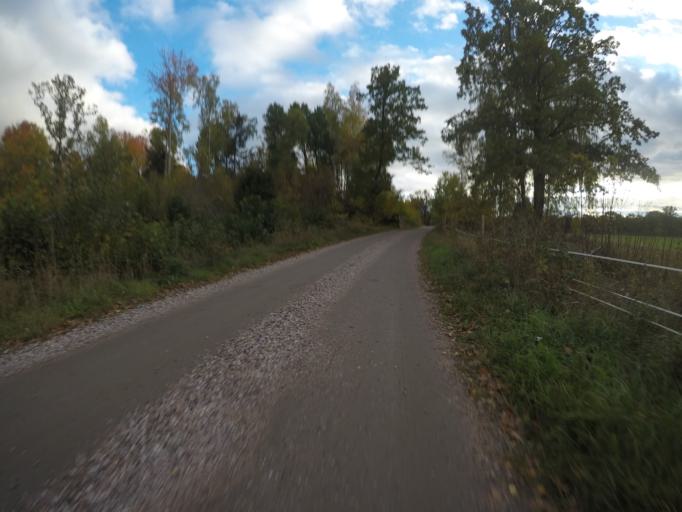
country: SE
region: Vaestmanland
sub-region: Arboga Kommun
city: Tyringe
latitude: 59.3005
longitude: 16.0052
